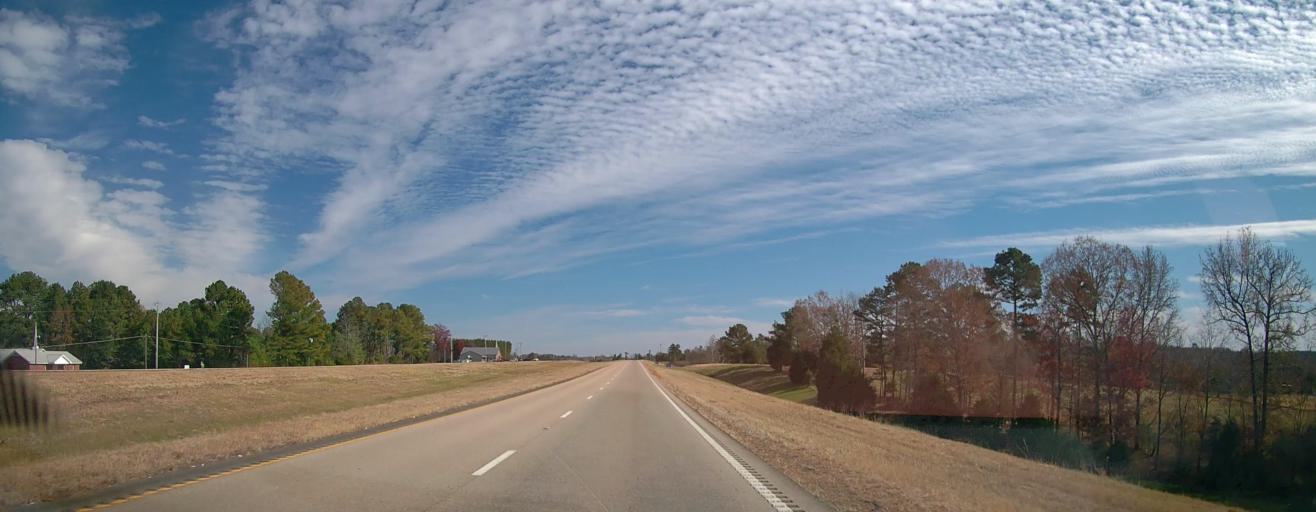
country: US
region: Mississippi
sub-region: Benton County
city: Ashland
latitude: 34.9534
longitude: -89.0133
